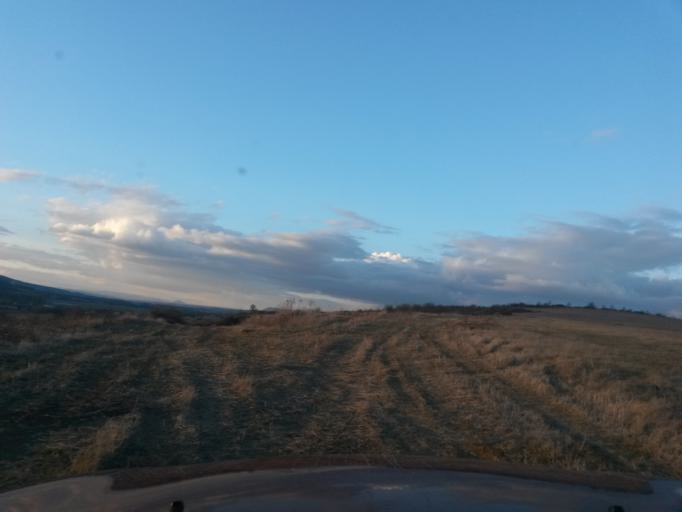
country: SK
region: Kosicky
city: Kosice
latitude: 48.6966
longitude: 21.3484
